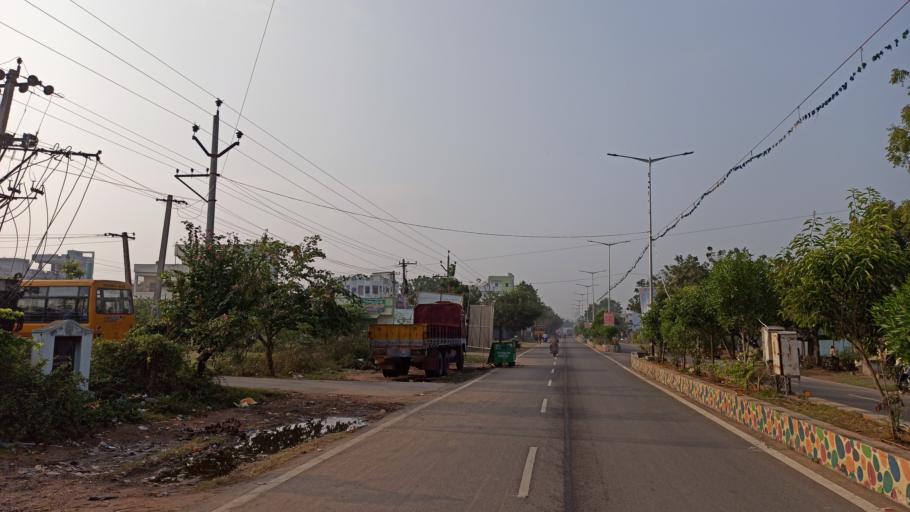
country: IN
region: Andhra Pradesh
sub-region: Guntur
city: Narasaraopet
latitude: 16.2507
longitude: 80.0573
